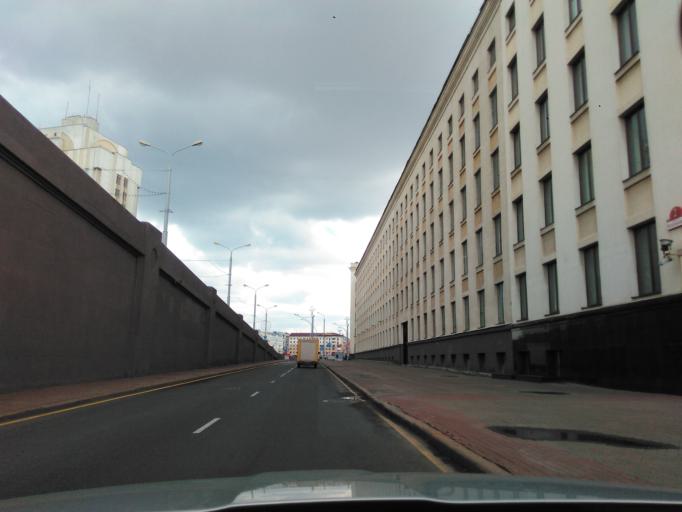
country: BY
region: Minsk
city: Minsk
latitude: 53.8928
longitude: 27.5442
